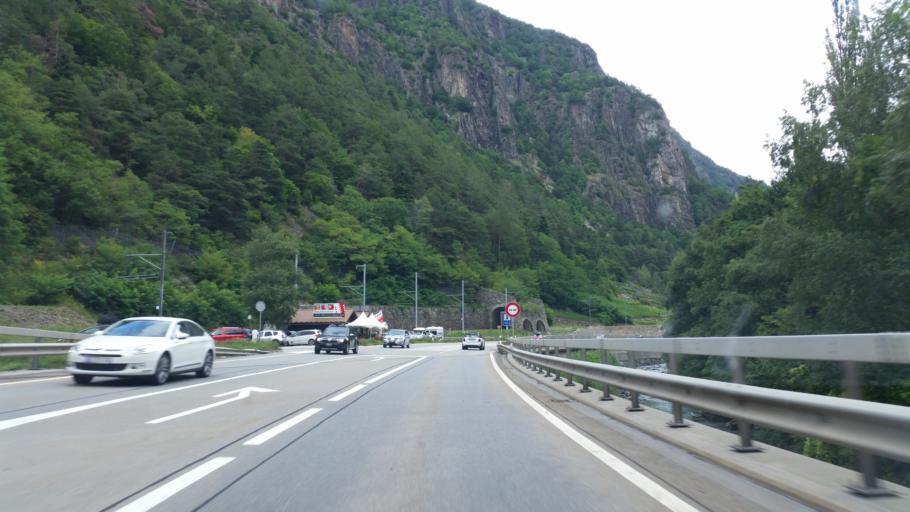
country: CH
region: Valais
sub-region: Martigny District
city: Martigny-Ville
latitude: 46.0818
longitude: 7.0936
